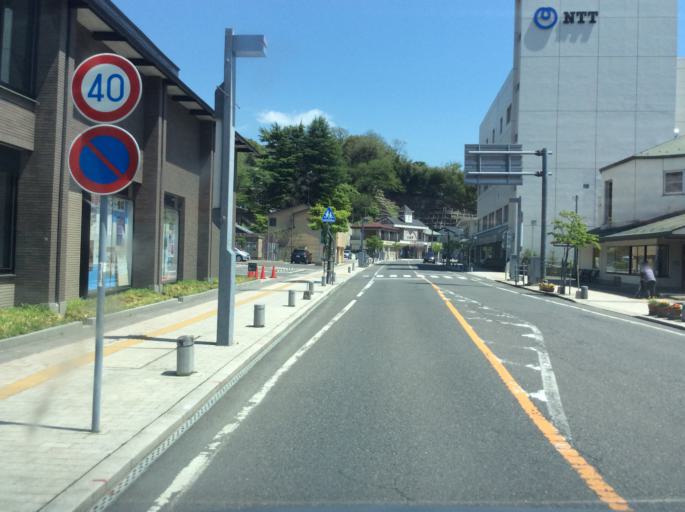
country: JP
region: Fukushima
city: Miharu
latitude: 37.4420
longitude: 140.4911
